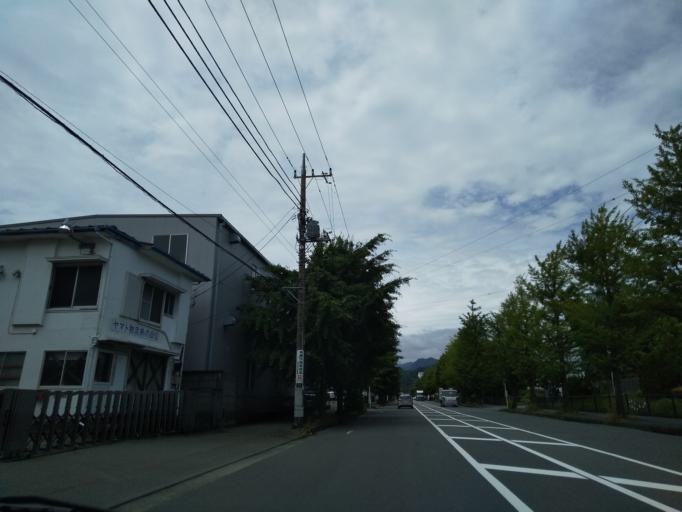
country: JP
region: Kanagawa
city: Zama
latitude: 35.5086
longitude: 139.3497
